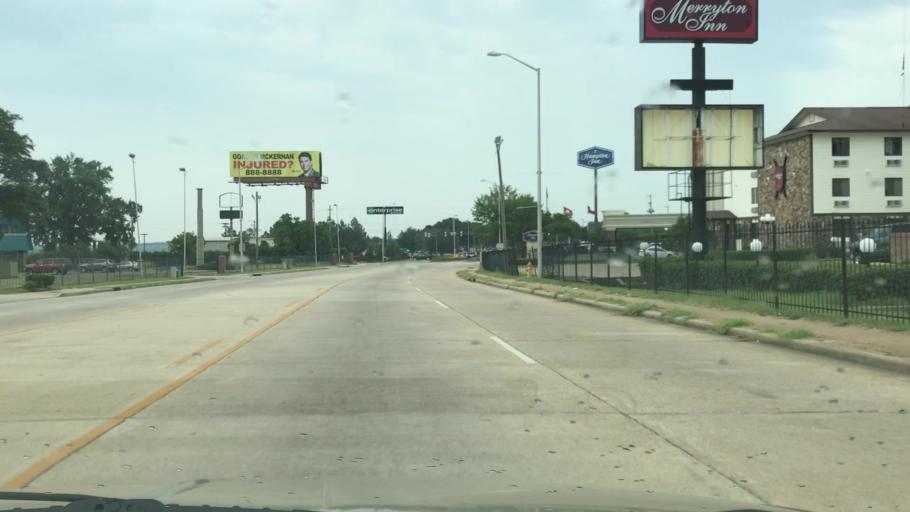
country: US
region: Louisiana
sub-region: Caddo Parish
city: Shreveport
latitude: 32.4585
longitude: -93.8272
